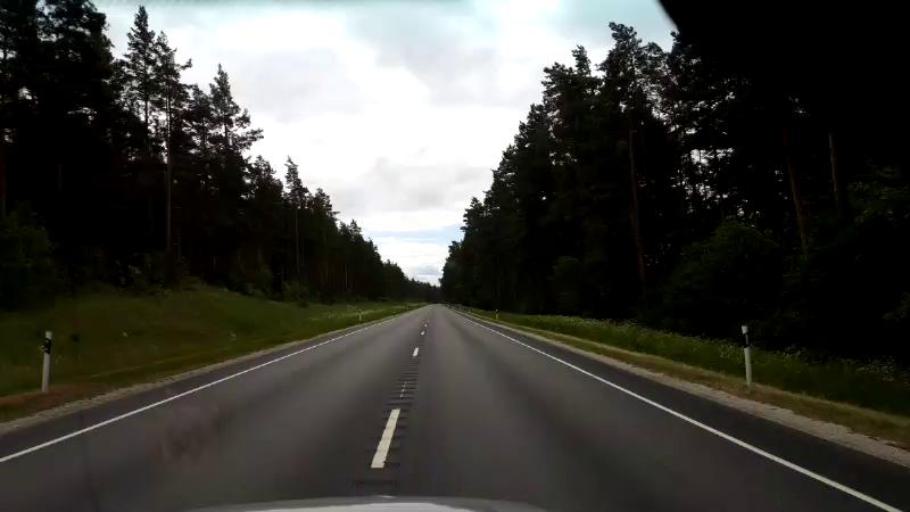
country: EE
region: Paernumaa
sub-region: Paernu linn
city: Parnu
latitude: 58.1586
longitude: 24.4984
